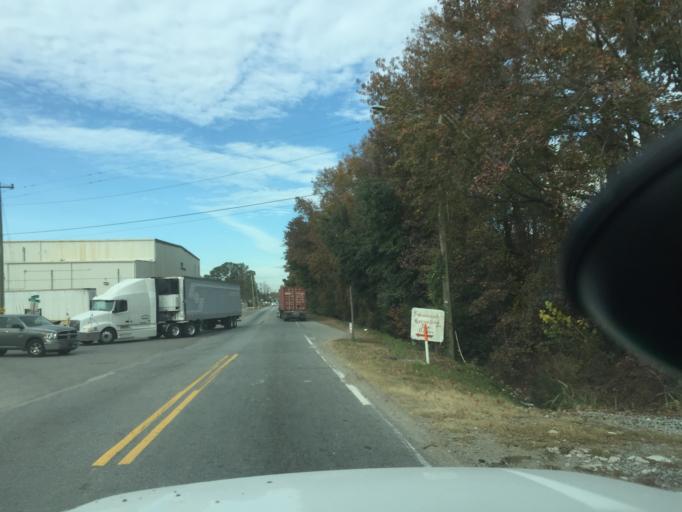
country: US
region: Georgia
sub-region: Chatham County
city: Savannah
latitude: 32.0849
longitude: -81.1340
